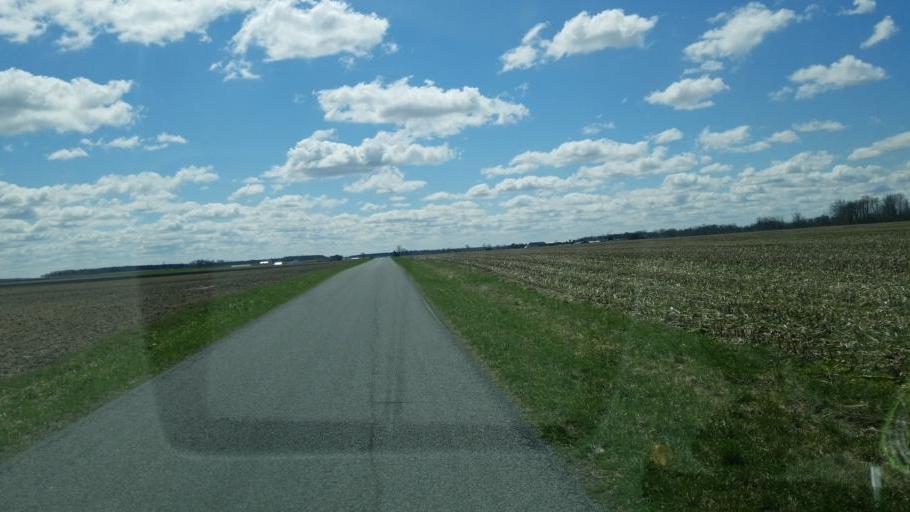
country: US
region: Ohio
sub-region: Seneca County
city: Fostoria
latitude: 41.0753
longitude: -83.5147
